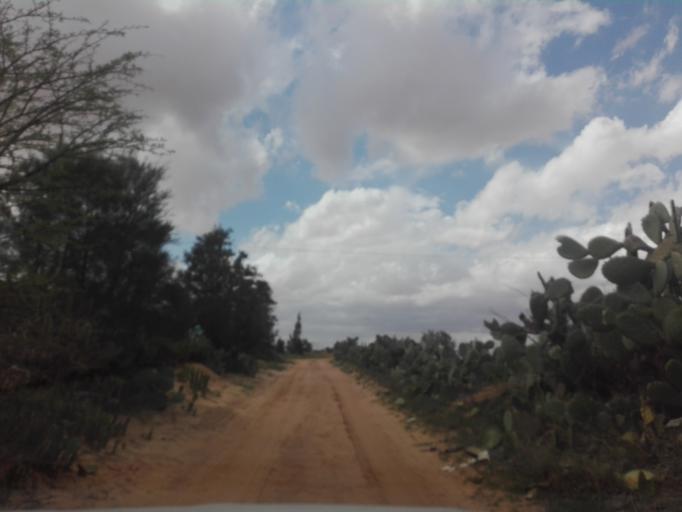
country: TN
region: Safaqis
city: Sfax
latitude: 34.6954
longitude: 10.4459
